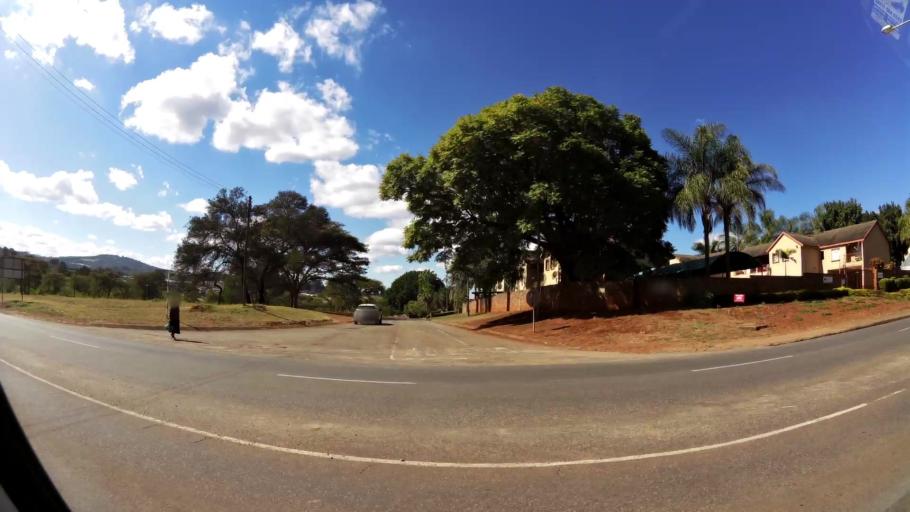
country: ZA
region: Limpopo
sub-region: Mopani District Municipality
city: Tzaneen
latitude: -23.8181
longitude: 30.1584
